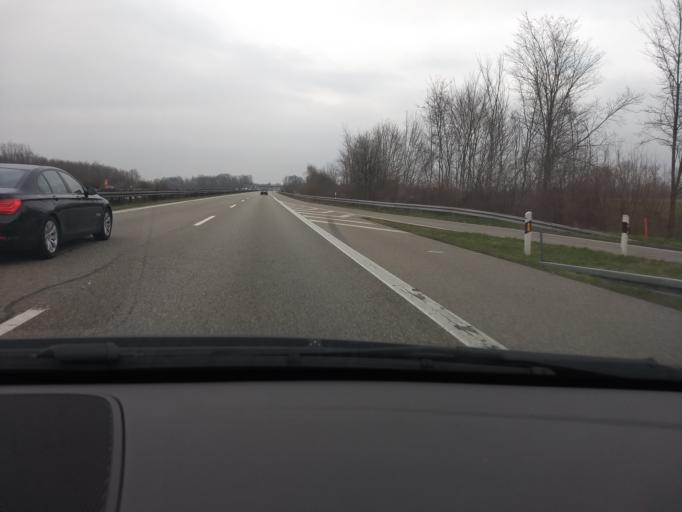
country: DE
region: Baden-Wuerttemberg
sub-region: Freiburg Region
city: Kenzingen
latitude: 48.2002
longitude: 7.7458
